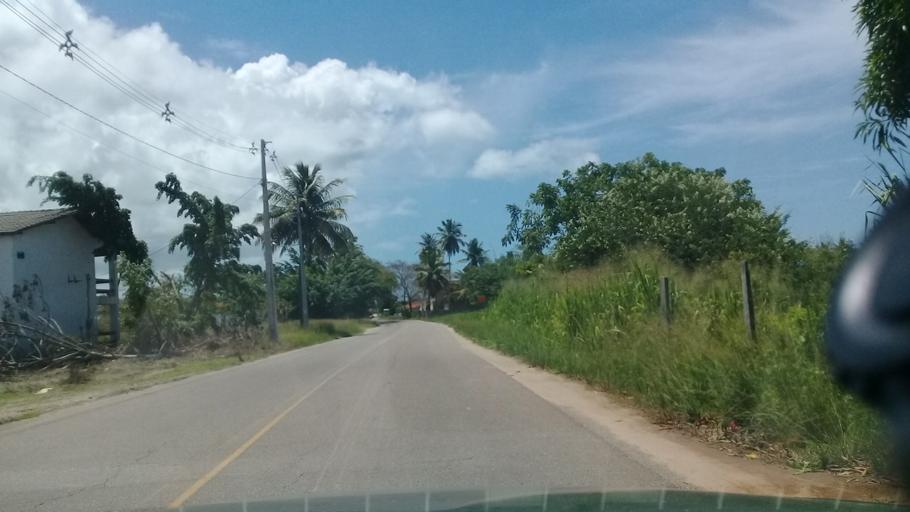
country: BR
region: Pernambuco
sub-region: Sirinhaem
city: Sirinhaem
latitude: -8.6237
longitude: -35.0632
